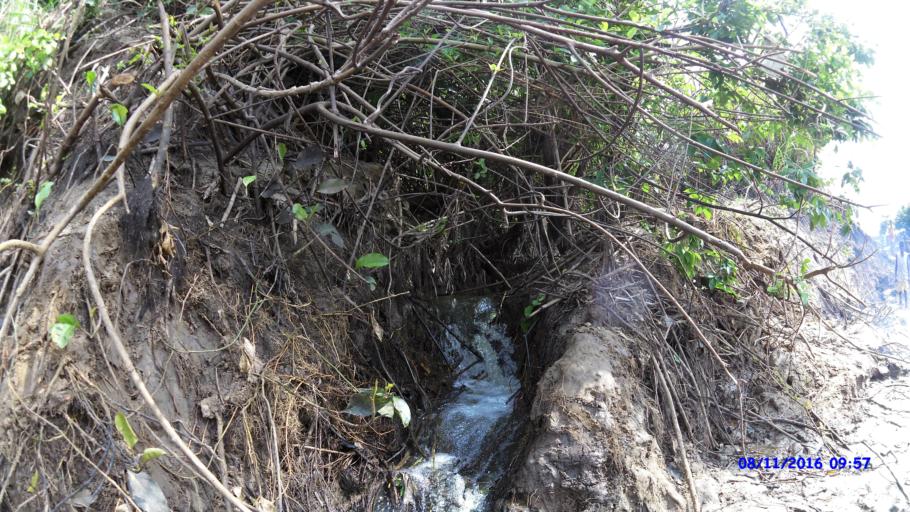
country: BJ
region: Mono
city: Come
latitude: 6.4400
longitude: 1.7641
